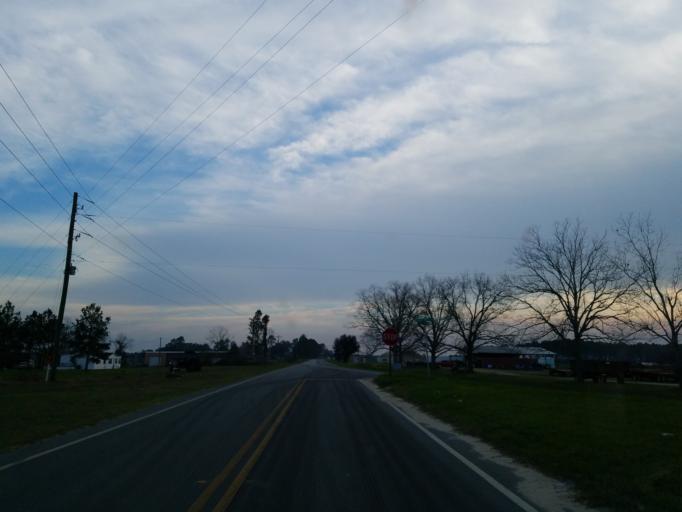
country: US
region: Georgia
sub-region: Tift County
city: Omega
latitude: 31.2052
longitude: -83.5824
